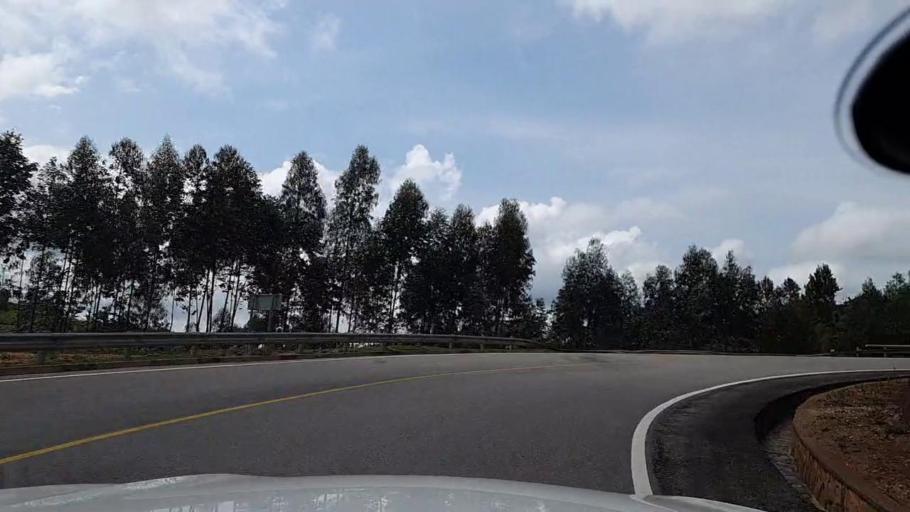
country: RW
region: Southern Province
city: Nzega
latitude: -2.5202
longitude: 29.4591
